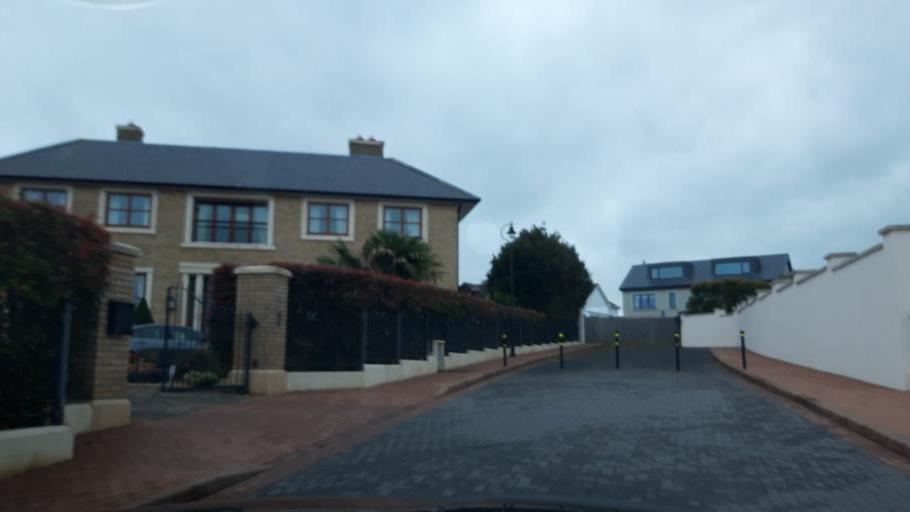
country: IE
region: Leinster
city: Malahide
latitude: 53.4458
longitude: -6.1473
